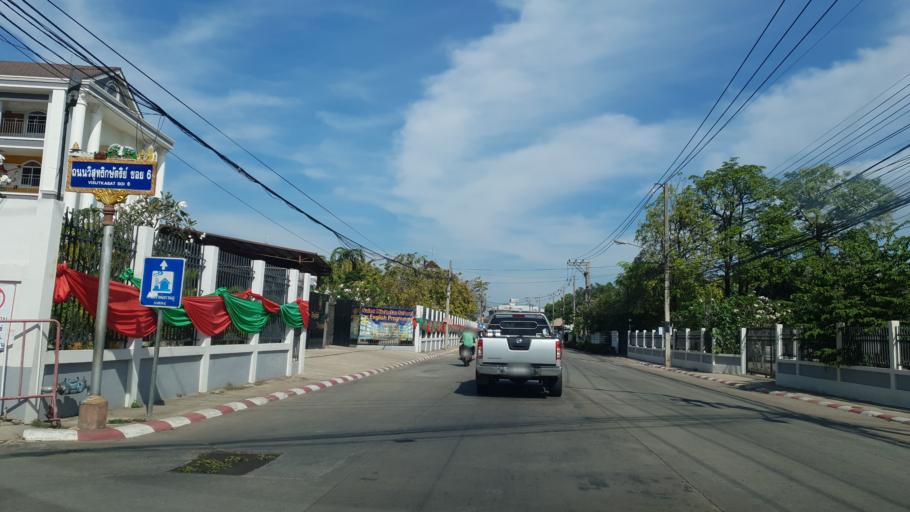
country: TH
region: Phitsanulok
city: Phitsanulok
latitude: 16.8128
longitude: 100.2678
